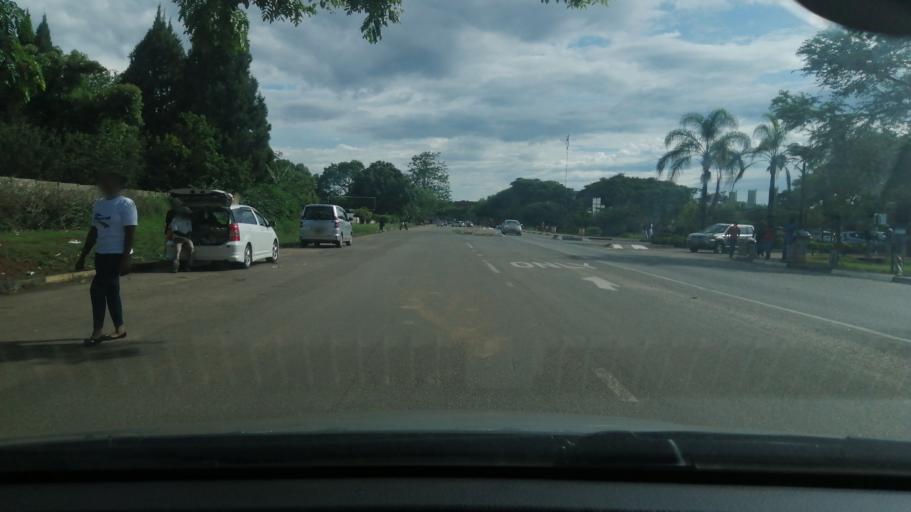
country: ZW
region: Harare
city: Harare
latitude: -17.7637
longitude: 30.9799
